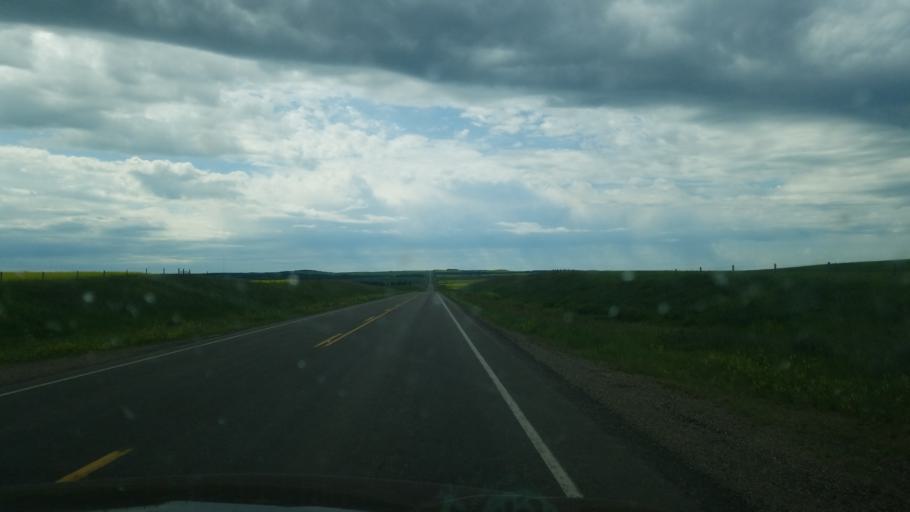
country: CA
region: Saskatchewan
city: Unity
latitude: 52.9167
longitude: -109.3425
